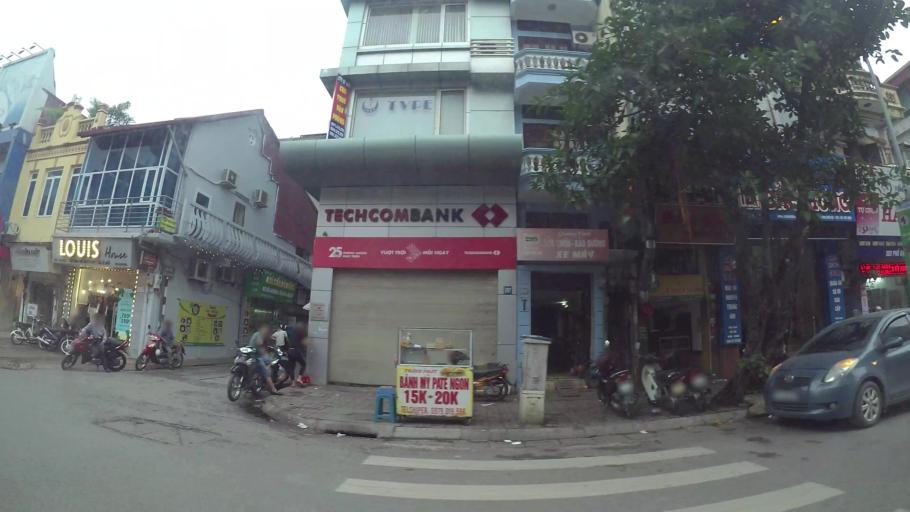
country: VN
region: Ha Noi
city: Hai BaTrung
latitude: 21.0022
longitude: 105.8508
